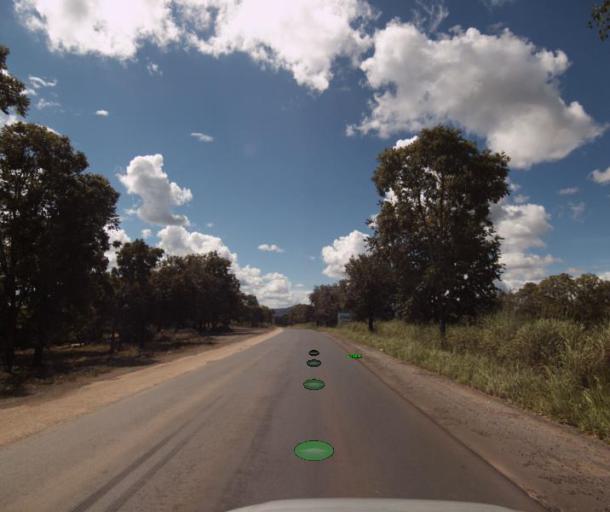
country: BR
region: Goias
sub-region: Porangatu
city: Porangatu
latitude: -13.7073
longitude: -49.0209
